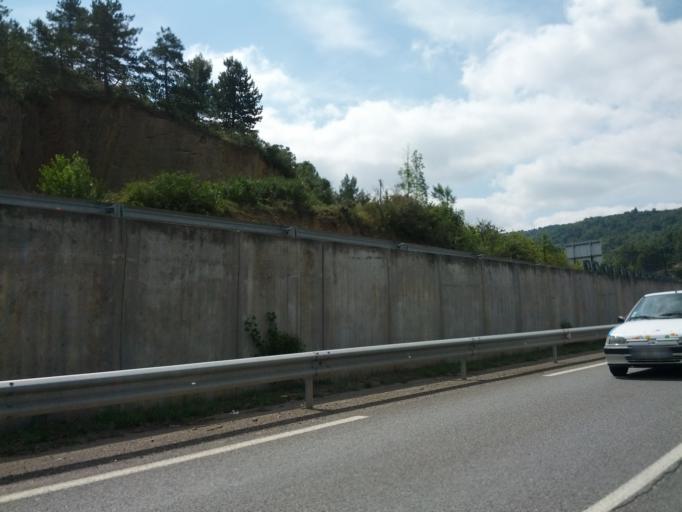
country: FR
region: Languedoc-Roussillon
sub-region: Departement de l'Aude
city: Esperaza
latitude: 42.9360
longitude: 2.2352
